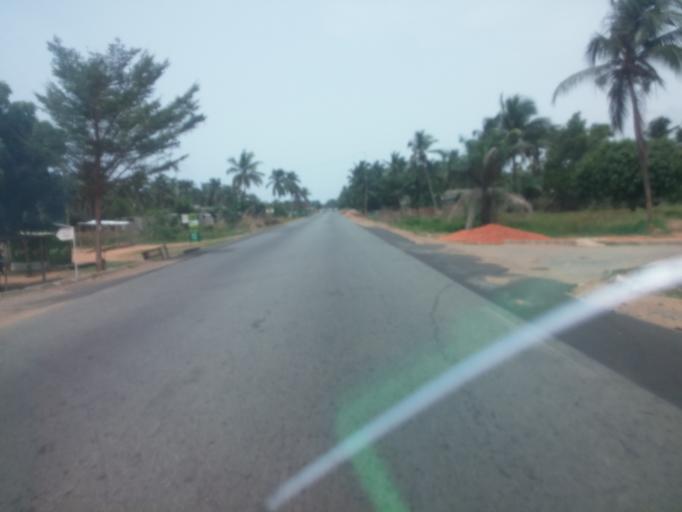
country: TG
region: Maritime
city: Vogan
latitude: 6.2120
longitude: 1.4332
